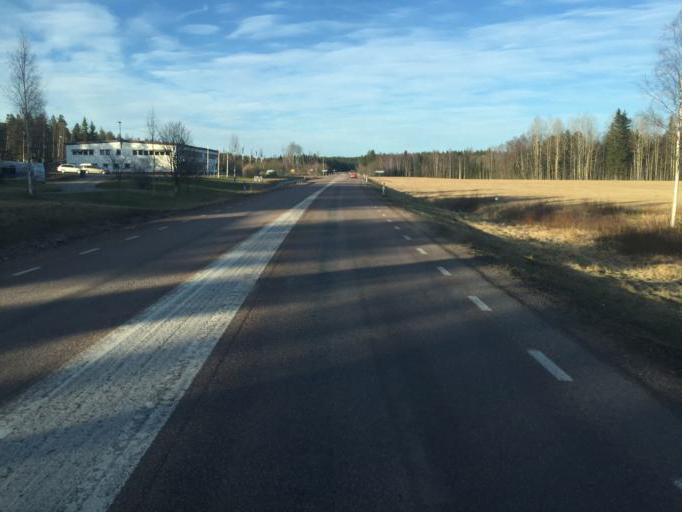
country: SE
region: Dalarna
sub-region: Gagnefs Kommun
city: Mockfjard
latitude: 60.5114
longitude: 14.9681
